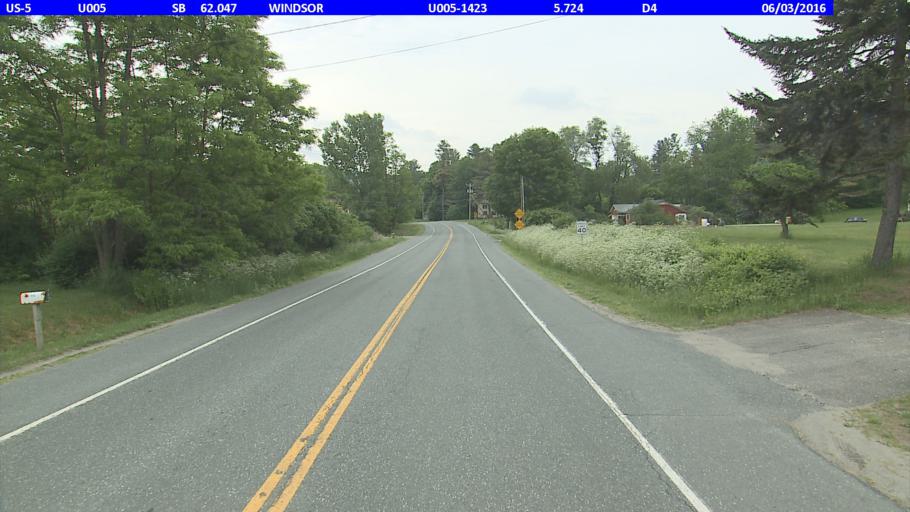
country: US
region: Vermont
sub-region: Windsor County
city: Windsor
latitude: 43.5053
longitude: -72.3999
